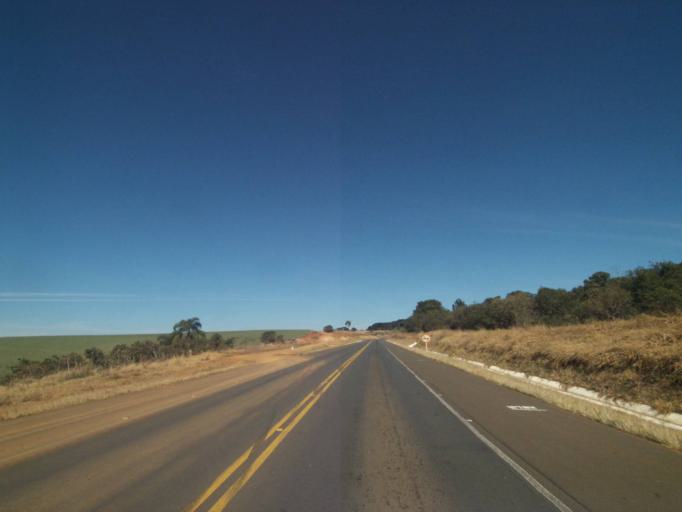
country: BR
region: Parana
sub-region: Tibagi
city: Tibagi
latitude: -24.6904
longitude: -50.4402
